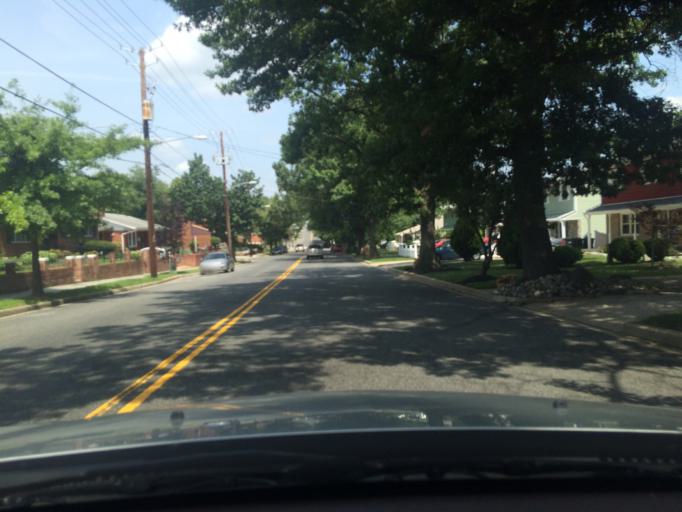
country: US
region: Maryland
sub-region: Prince George's County
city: Chillum
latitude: 38.9557
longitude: -76.9897
